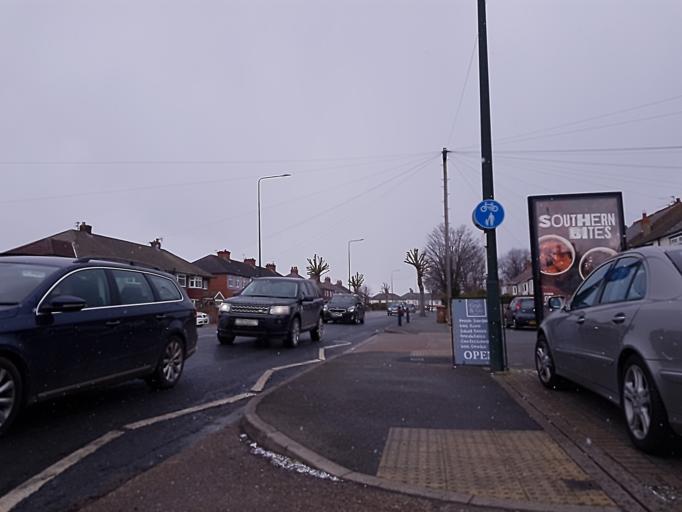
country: GB
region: England
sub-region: North East Lincolnshire
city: Grimbsy
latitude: 53.5626
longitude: -0.1113
